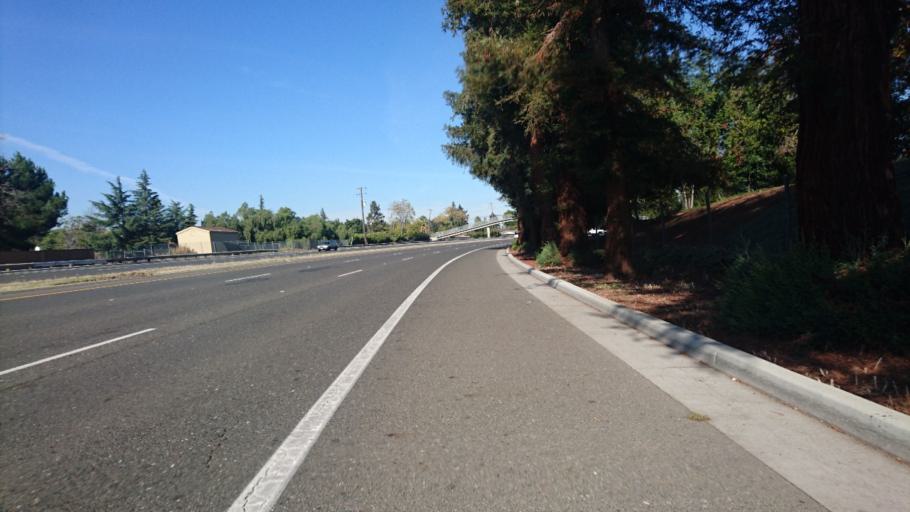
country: US
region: California
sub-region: Santa Clara County
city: Campbell
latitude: 37.2827
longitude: -121.9600
